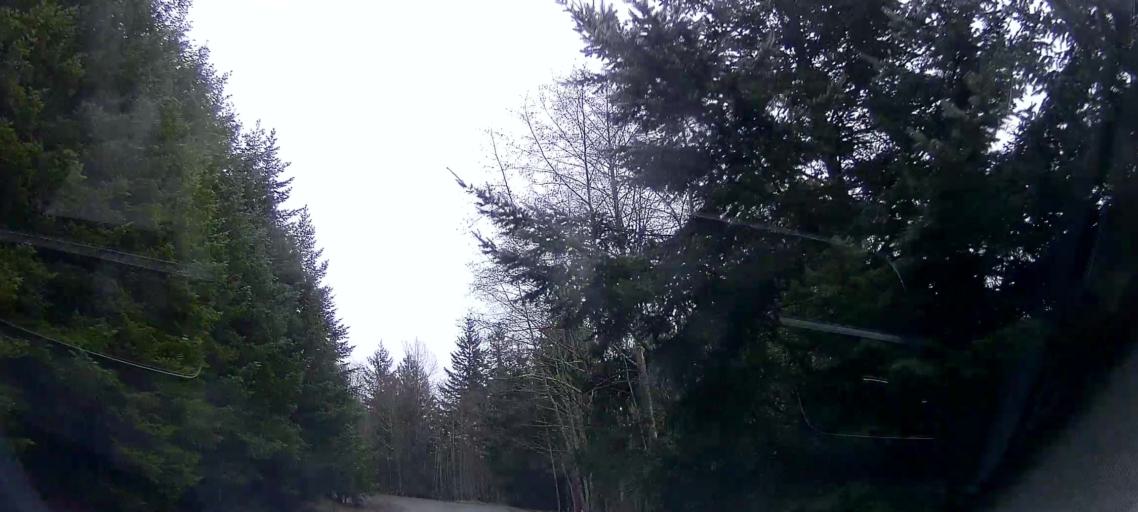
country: US
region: Washington
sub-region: Skagit County
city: Big Lake
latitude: 48.3836
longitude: -122.2919
